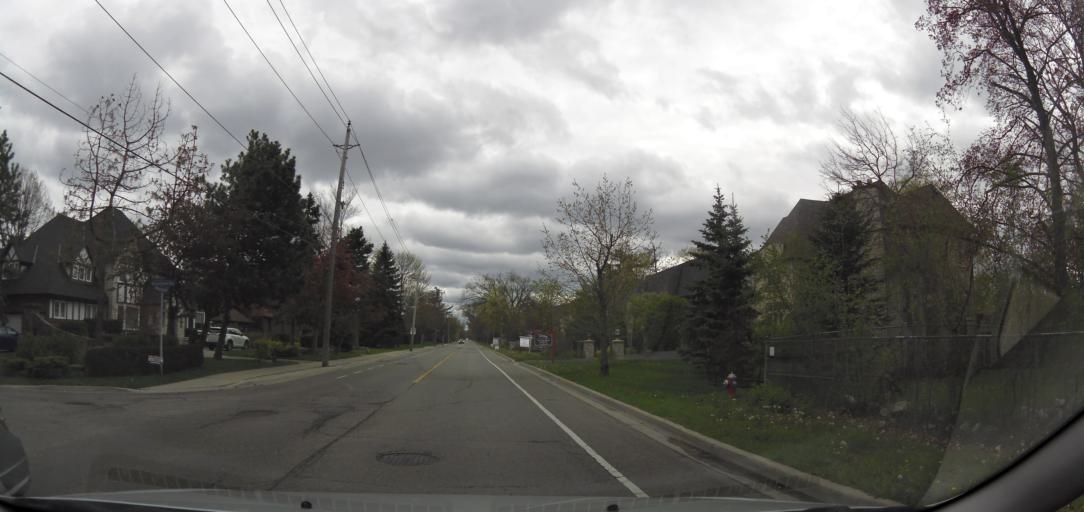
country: CA
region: Ontario
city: Mississauga
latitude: 43.5471
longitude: -79.6275
